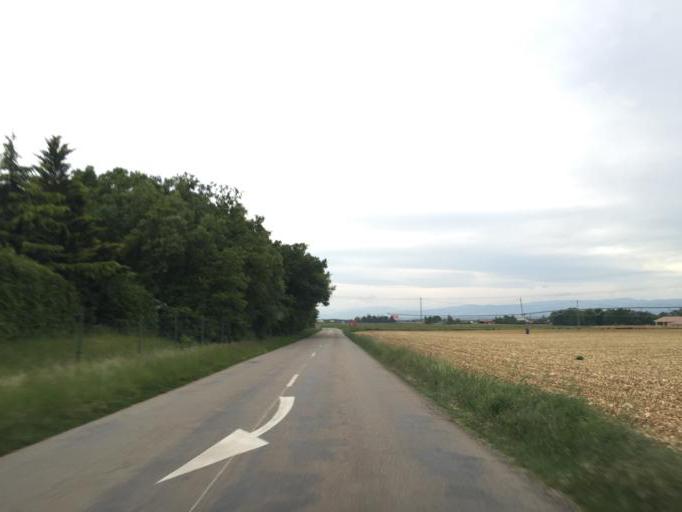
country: FR
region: Rhone-Alpes
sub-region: Departement de la Drome
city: Montelier
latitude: 44.9200
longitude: 5.0506
